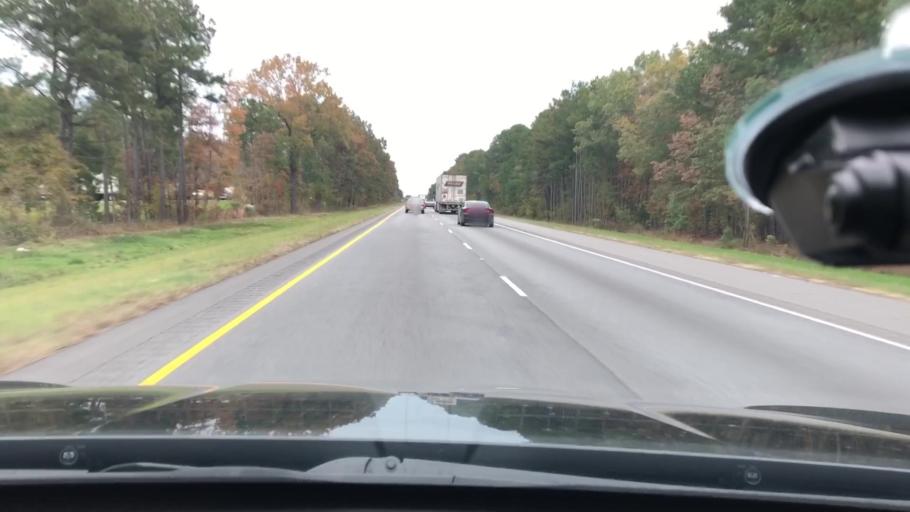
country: US
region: Arkansas
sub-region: Hempstead County
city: Hope
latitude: 33.6217
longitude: -93.7797
